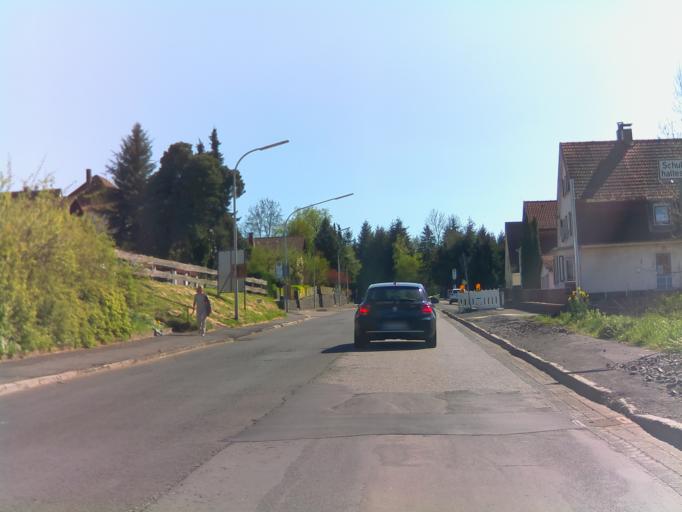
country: DE
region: Hesse
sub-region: Regierungsbezirk Giessen
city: Lauterbach
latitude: 50.6177
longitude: 9.3894
